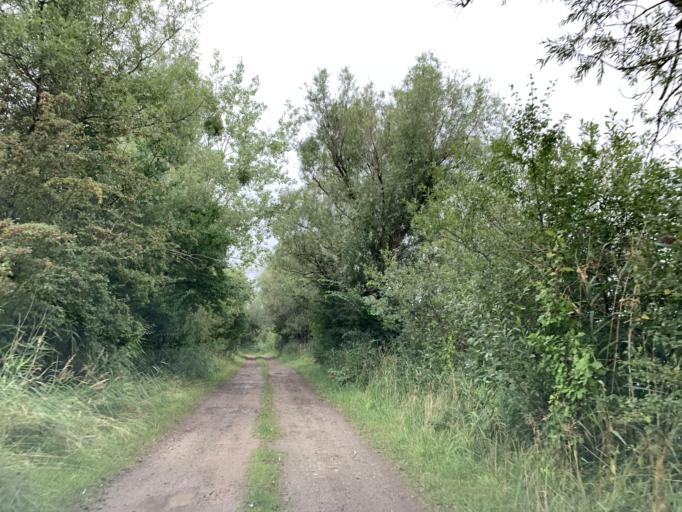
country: DE
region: Mecklenburg-Vorpommern
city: Carpin
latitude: 53.3893
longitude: 13.2334
